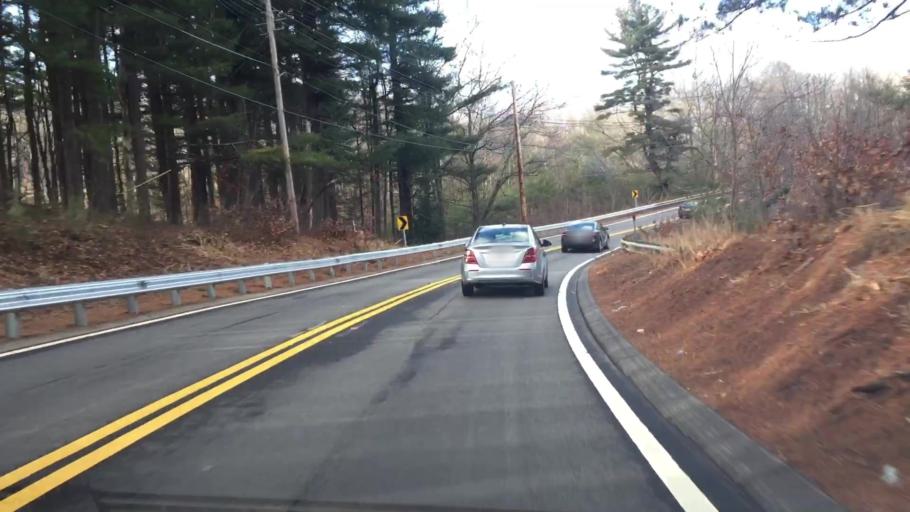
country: US
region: Massachusetts
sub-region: Worcester County
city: West Boylston
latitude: 42.3467
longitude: -71.7649
